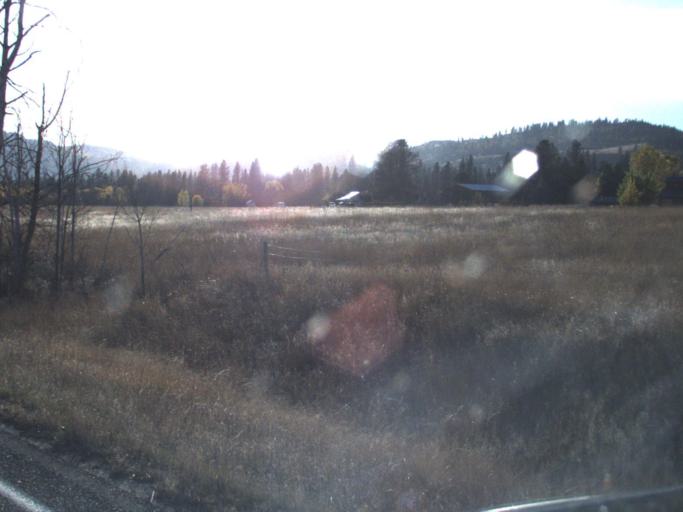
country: CA
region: British Columbia
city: Rossland
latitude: 48.8445
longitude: -117.9002
